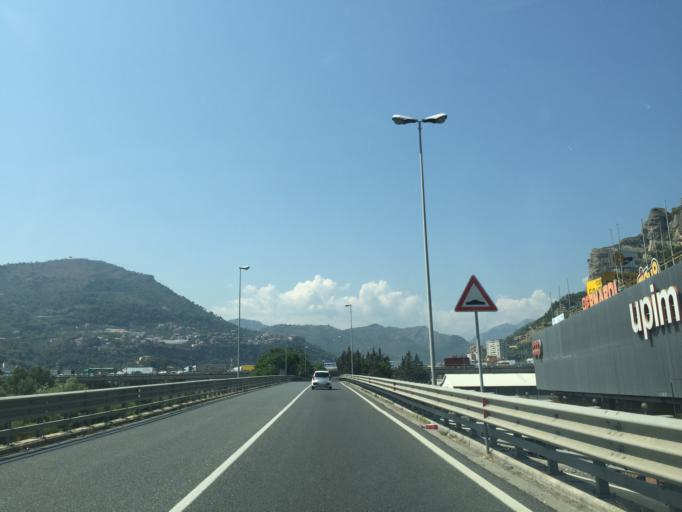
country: IT
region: Liguria
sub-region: Provincia di Imperia
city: Ventimiglia
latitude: 43.7992
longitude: 7.5995
